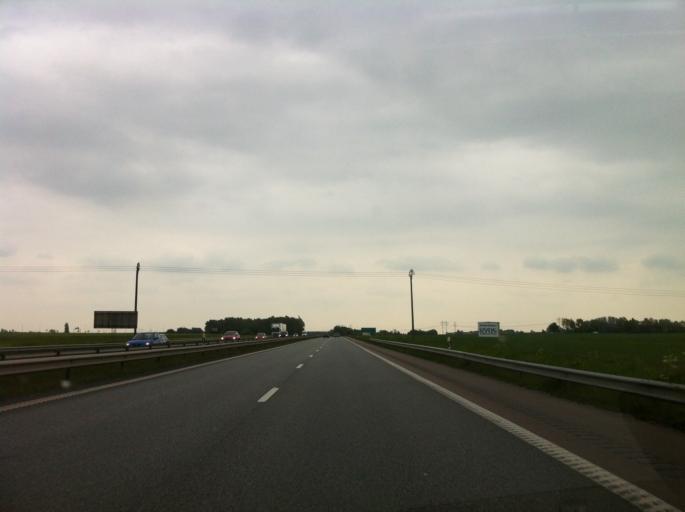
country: SE
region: Skane
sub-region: Kavlinge Kommun
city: Loddekopinge
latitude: 55.7506
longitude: 13.0114
